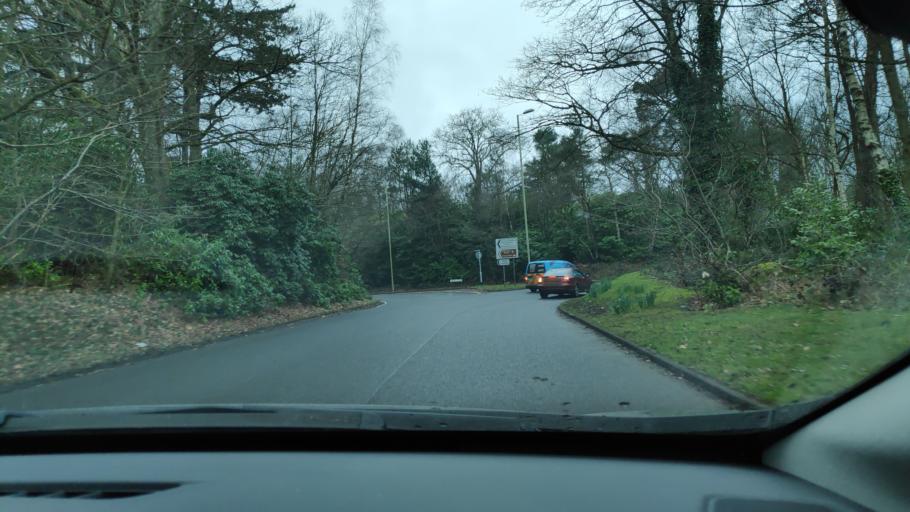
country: GB
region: England
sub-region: Hampshire
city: Aldershot
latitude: 51.2505
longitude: -0.7789
